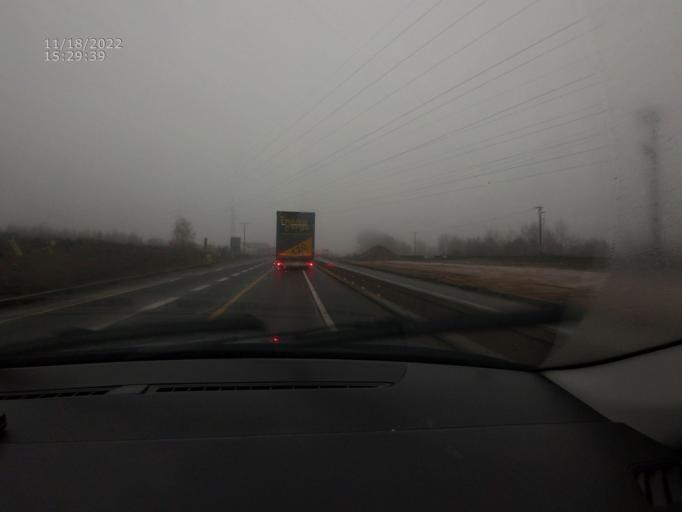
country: CZ
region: Central Bohemia
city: Milin
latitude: 49.6490
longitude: 14.0525
